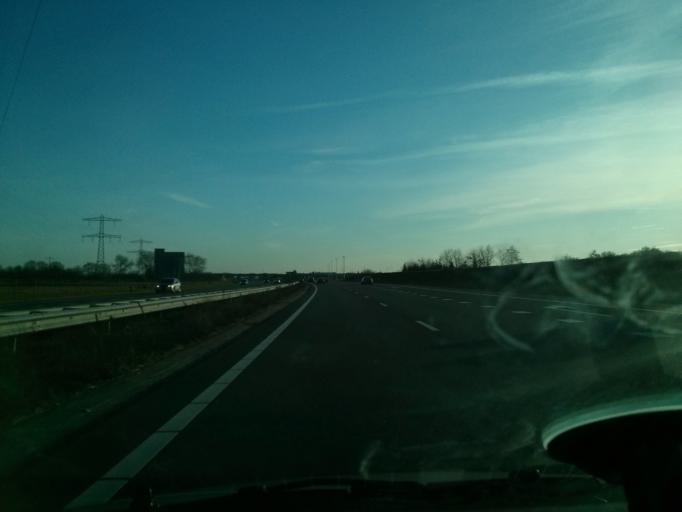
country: NL
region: North Brabant
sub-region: Gemeente Bernheze
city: Heesch
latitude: 51.7209
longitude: 5.5694
